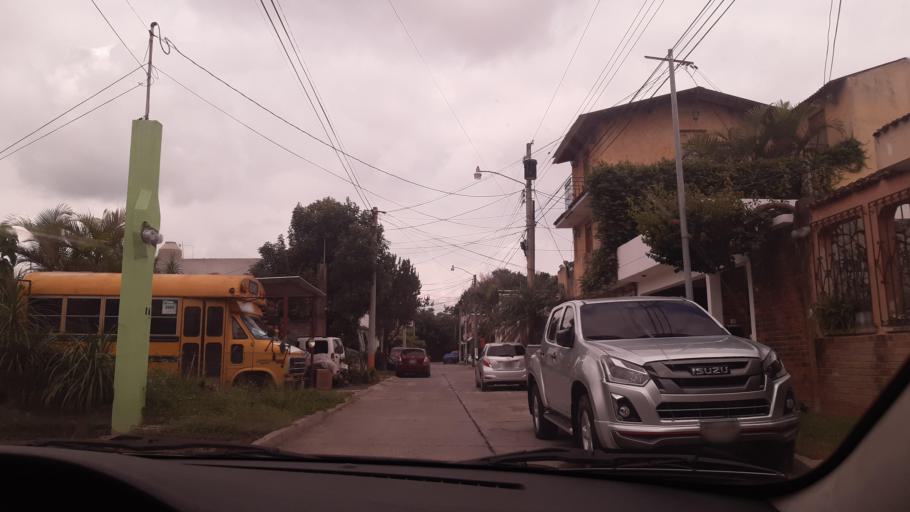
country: GT
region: Guatemala
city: Petapa
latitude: 14.5047
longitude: -90.5456
